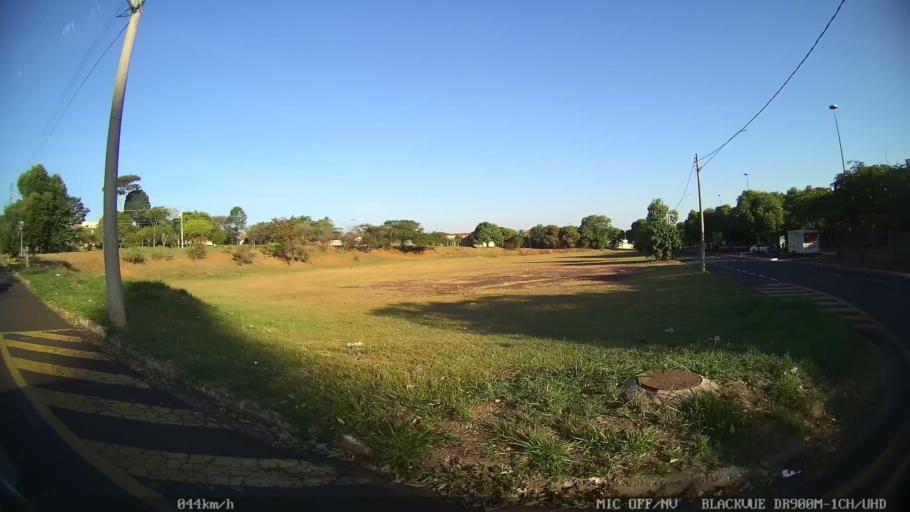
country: BR
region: Sao Paulo
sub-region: Sao Jose Do Rio Preto
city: Sao Jose do Rio Preto
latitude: -20.7991
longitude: -49.3589
